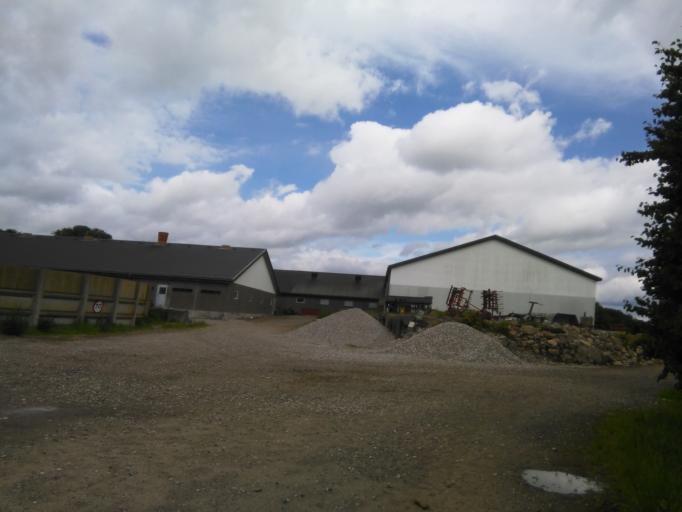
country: DK
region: Central Jutland
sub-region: Arhus Kommune
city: Logten
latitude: 56.2808
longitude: 10.3576
